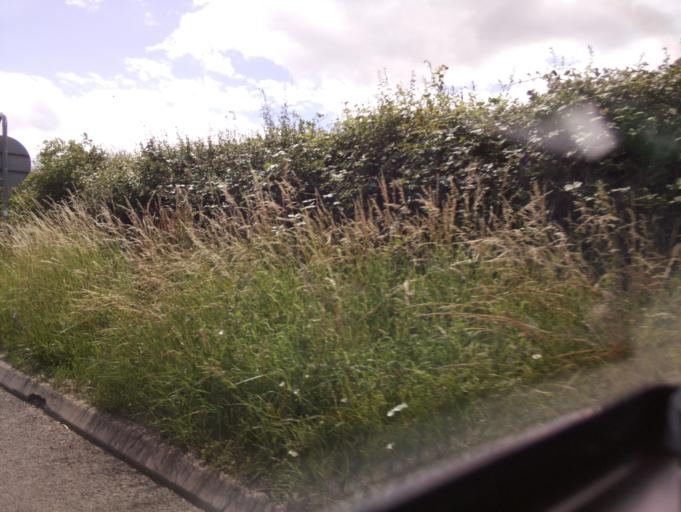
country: GB
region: England
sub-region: Nottinghamshire
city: Cotgrave
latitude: 52.8850
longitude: -1.0848
